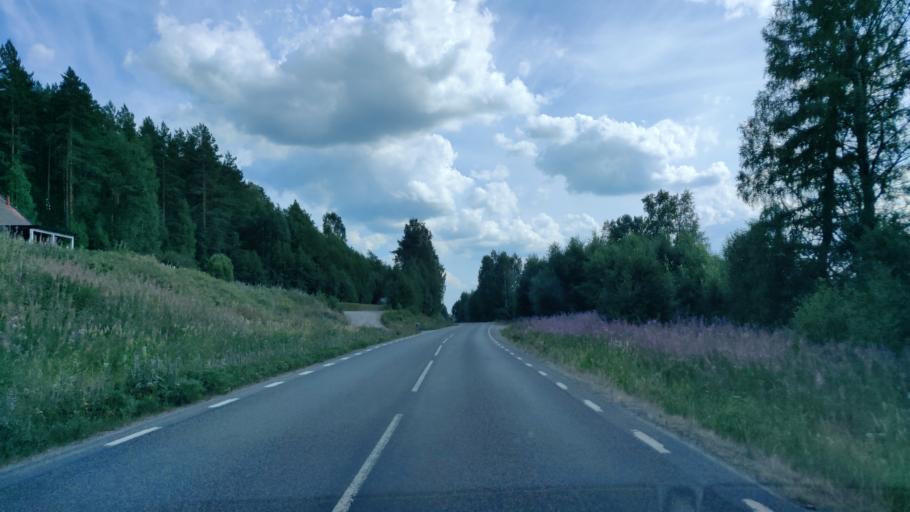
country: SE
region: Vaermland
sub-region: Hagfors Kommun
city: Ekshaerad
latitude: 60.1691
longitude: 13.5299
